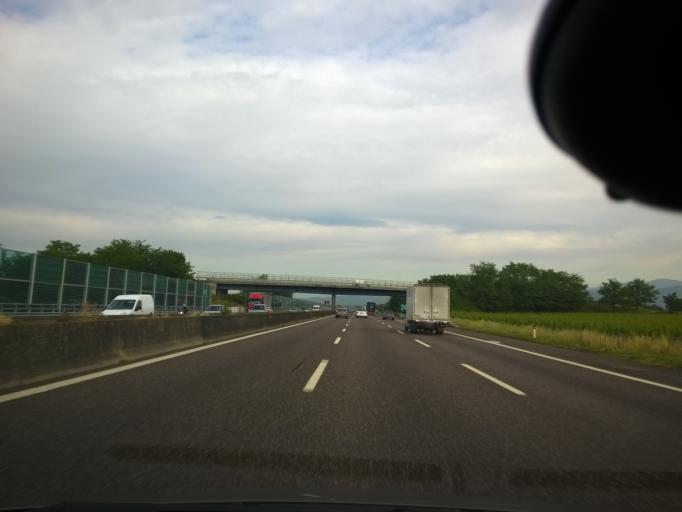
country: IT
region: Lombardy
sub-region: Provincia di Brescia
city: Adro
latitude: 45.6067
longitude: 9.9435
